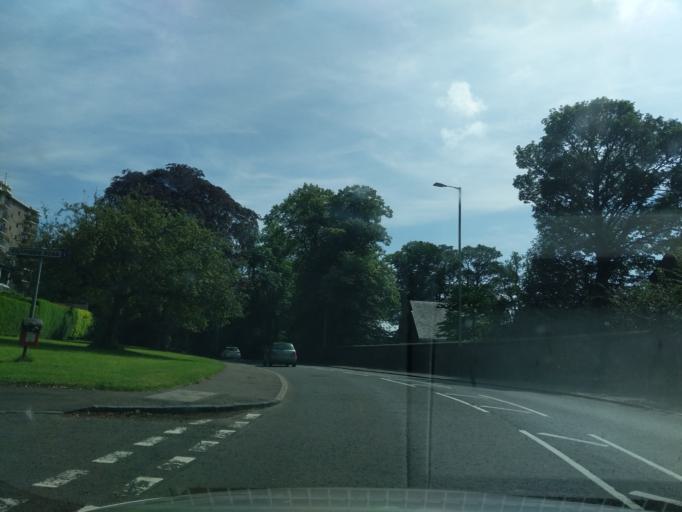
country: GB
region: Scotland
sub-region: Dundee City
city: Dundee
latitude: 56.4791
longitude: -3.0191
